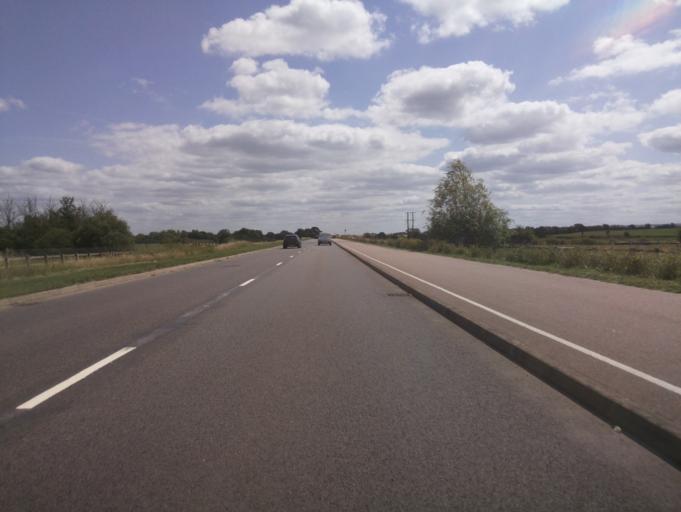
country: GB
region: England
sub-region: Buckinghamshire
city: Aylesbury
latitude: 51.8391
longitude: -0.8390
